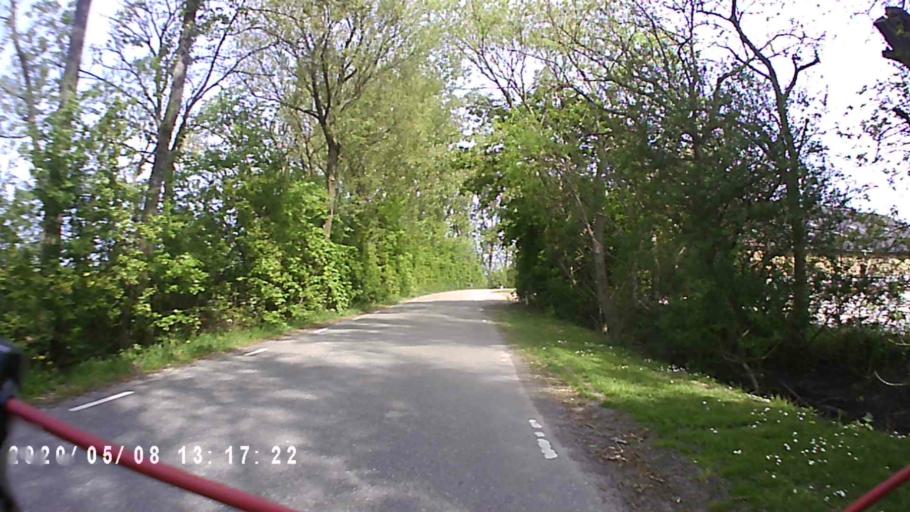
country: NL
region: Groningen
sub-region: Gemeente Bedum
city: Bedum
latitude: 53.3092
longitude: 6.7084
